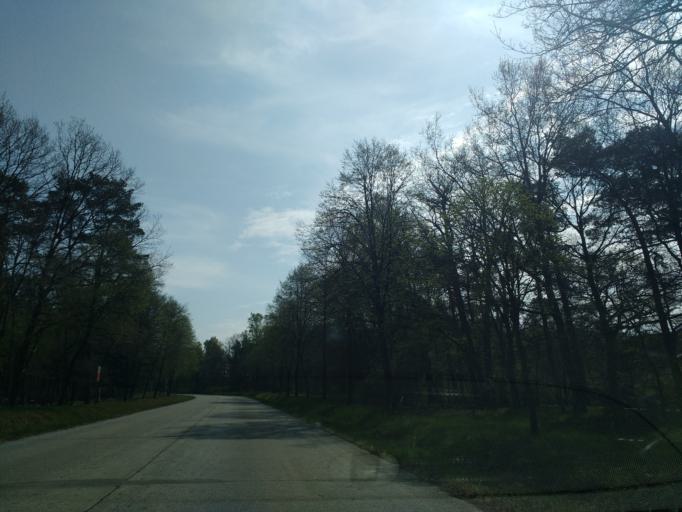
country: DE
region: North Rhine-Westphalia
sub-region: Regierungsbezirk Detmold
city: Hovelhof
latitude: 51.8267
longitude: 8.7097
